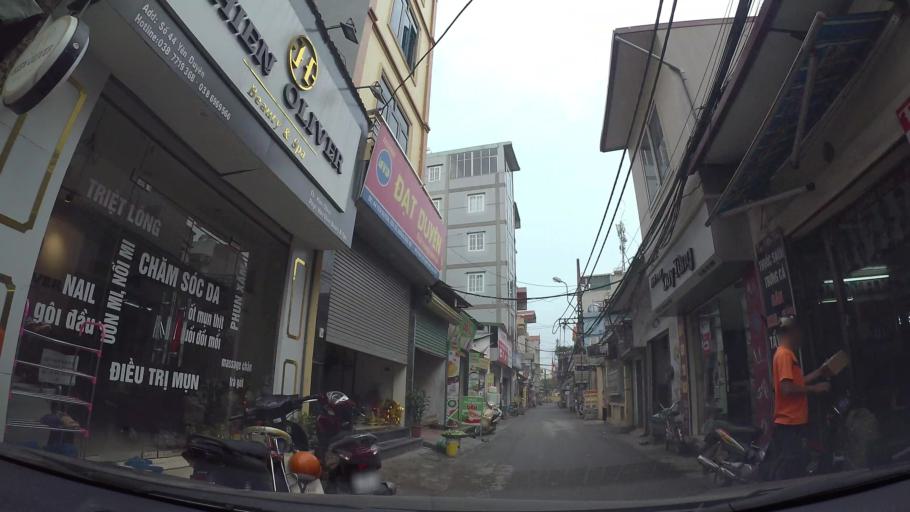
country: VN
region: Ha Noi
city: Van Dien
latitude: 20.9728
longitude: 105.8680
